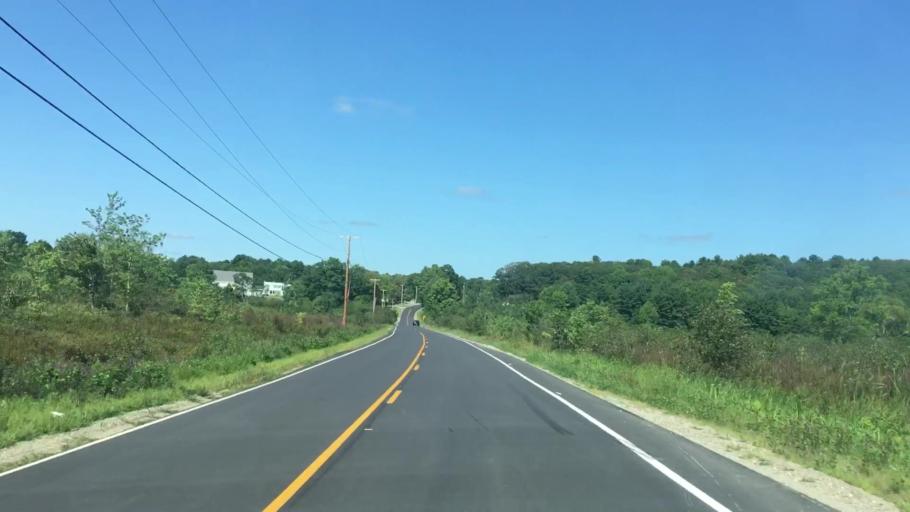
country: US
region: Maine
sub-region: Sagadahoc County
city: Topsham
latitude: 43.9774
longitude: -69.9809
